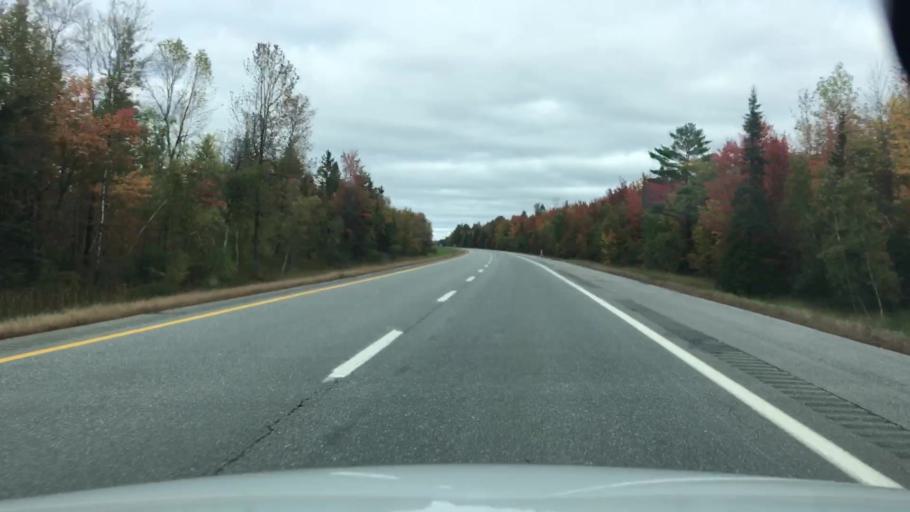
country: US
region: Maine
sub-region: Kennebec County
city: Clinton
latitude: 44.6671
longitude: -69.4902
